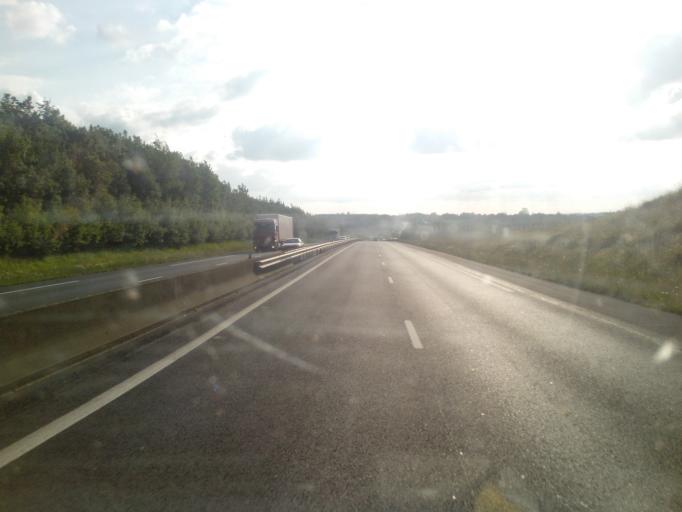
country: FR
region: Lower Normandy
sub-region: Departement du Calvados
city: Cahagnes
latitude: 49.0503
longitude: -0.7259
